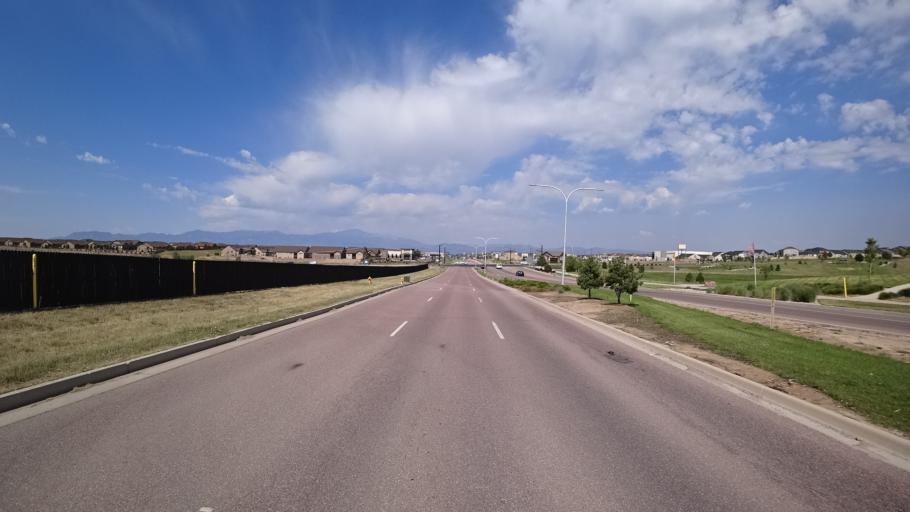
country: US
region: Colorado
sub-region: El Paso County
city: Cimarron Hills
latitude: 38.9265
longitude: -104.6806
